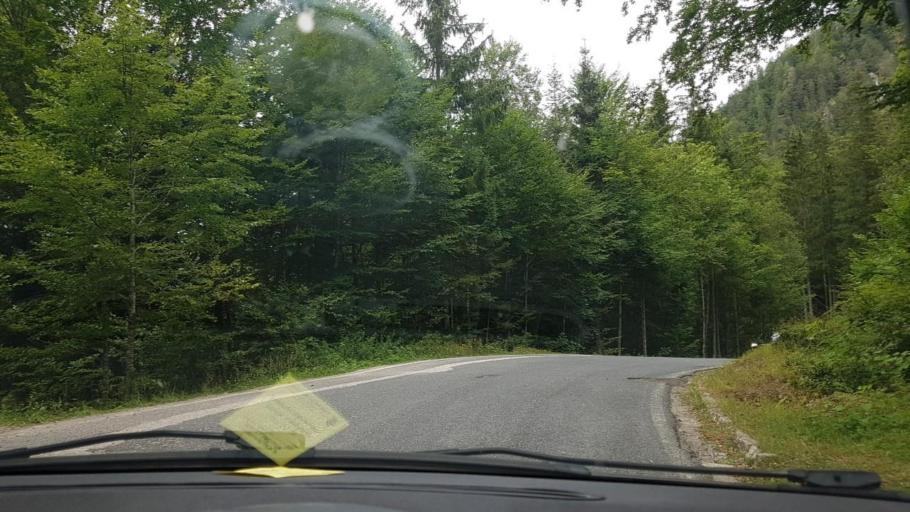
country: AT
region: Carinthia
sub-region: Politischer Bezirk Villach Land
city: Arnoldstein
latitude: 46.4772
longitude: 13.6720
